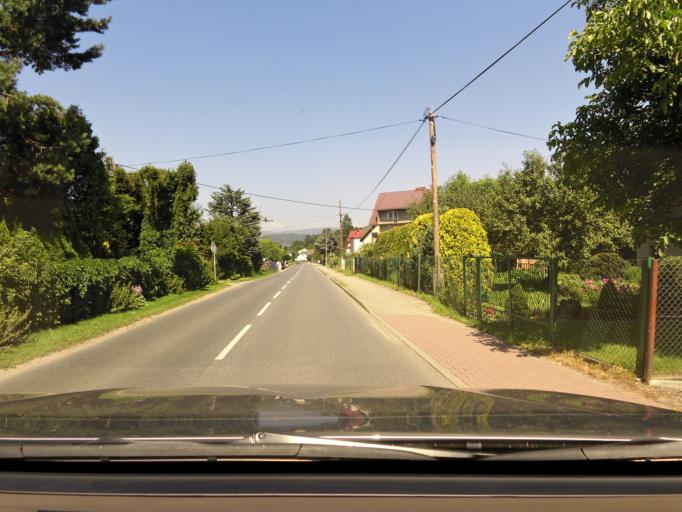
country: PL
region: Silesian Voivodeship
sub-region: Powiat zywiecki
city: Milowka
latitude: 49.5426
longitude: 19.1048
